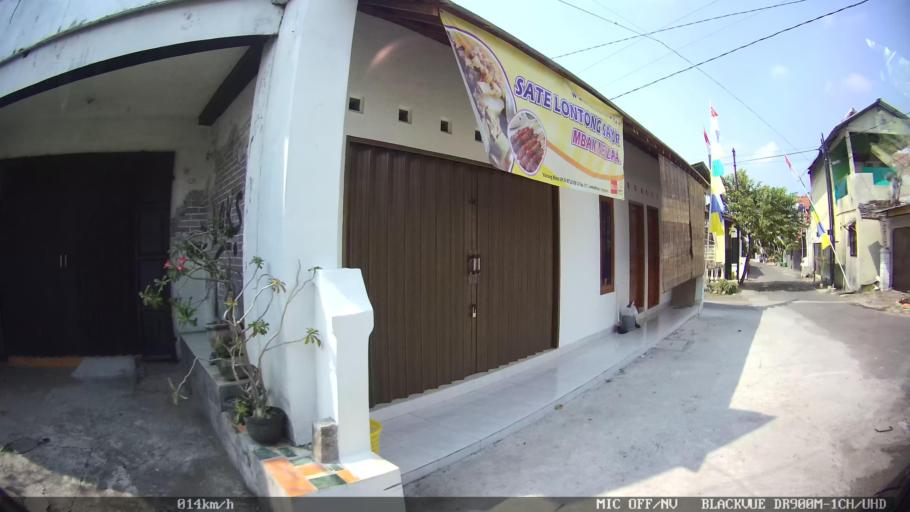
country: ID
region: Daerah Istimewa Yogyakarta
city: Yogyakarta
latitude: -7.8096
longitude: 110.3907
